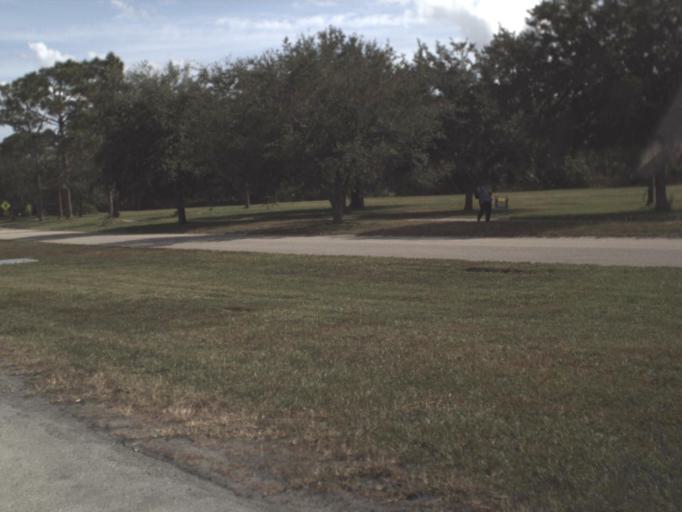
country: US
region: Florida
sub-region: Osceola County
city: Poinciana
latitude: 28.1459
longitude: -81.4649
